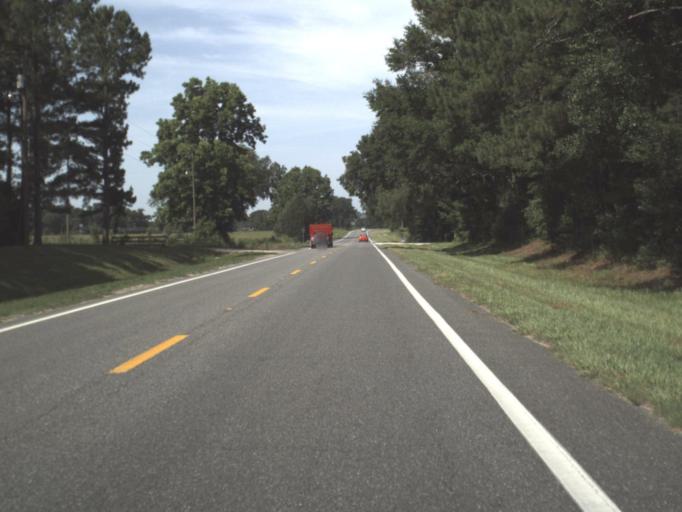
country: US
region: Florida
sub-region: Suwannee County
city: Live Oak
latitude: 30.2180
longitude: -83.0795
